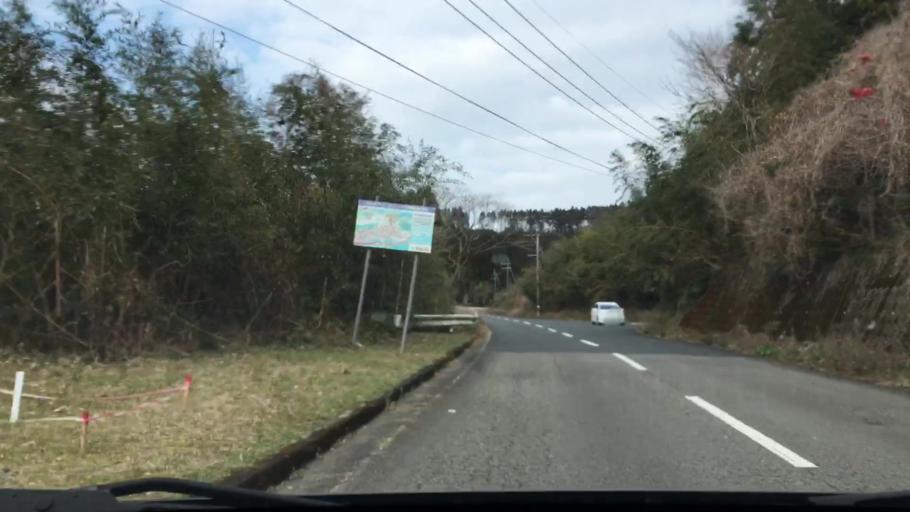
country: JP
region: Miyazaki
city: Nichinan
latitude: 31.6647
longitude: 131.3175
